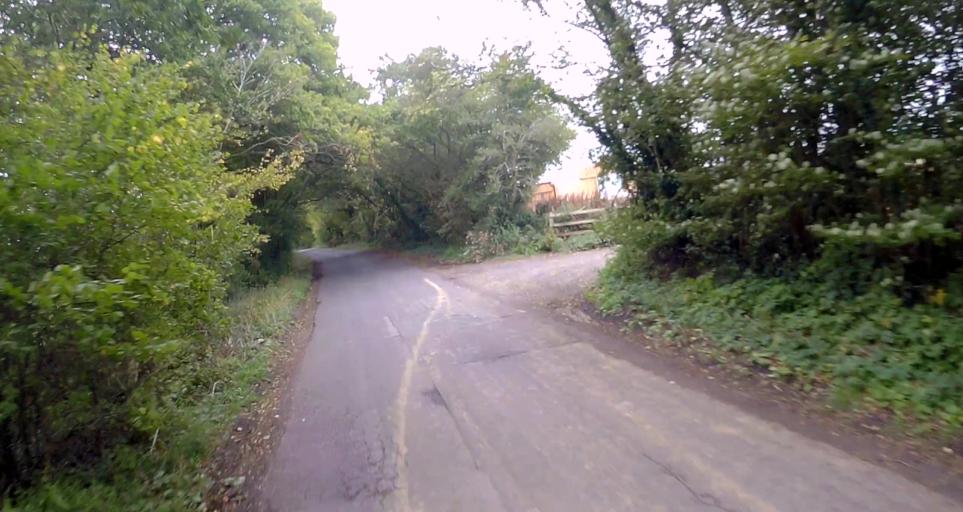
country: GB
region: England
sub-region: Hampshire
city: Four Marks
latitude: 51.1475
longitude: -1.0882
